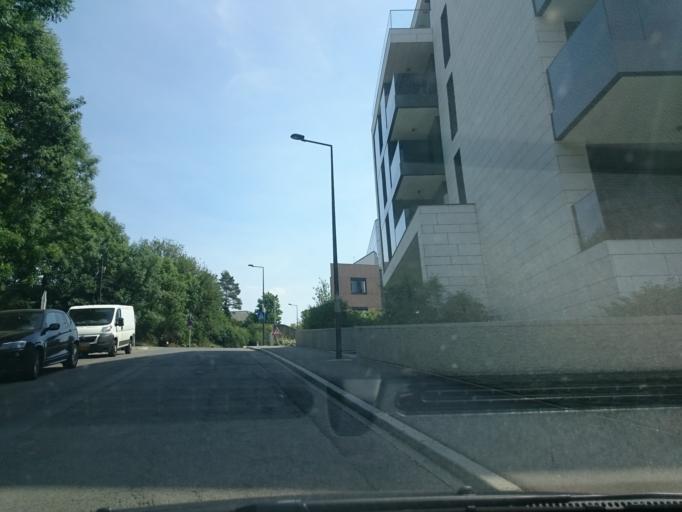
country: LU
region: Luxembourg
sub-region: Canton de Luxembourg
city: Luxembourg
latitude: 49.6036
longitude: 6.1058
